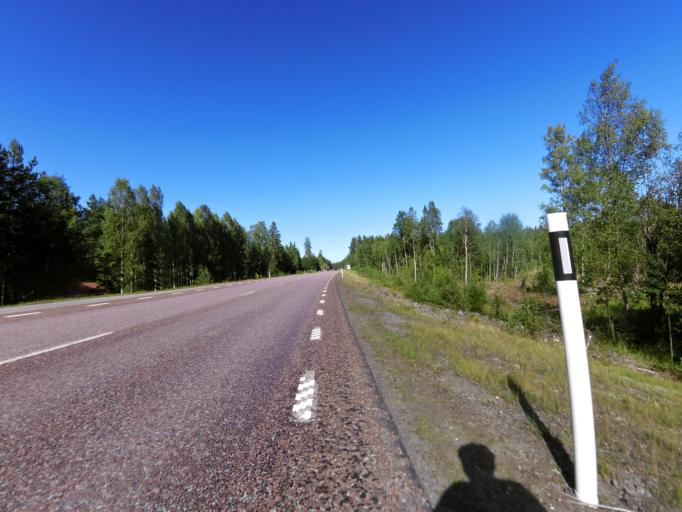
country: SE
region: Gaevleborg
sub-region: Hofors Kommun
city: Hofors
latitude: 60.5556
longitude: 16.4791
